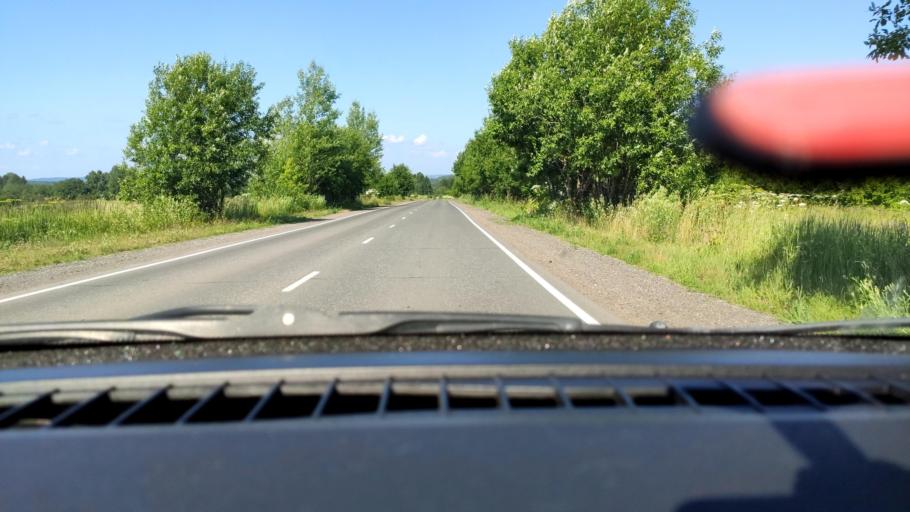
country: RU
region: Perm
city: Yugo-Kamskiy
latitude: 57.6878
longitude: 55.5564
